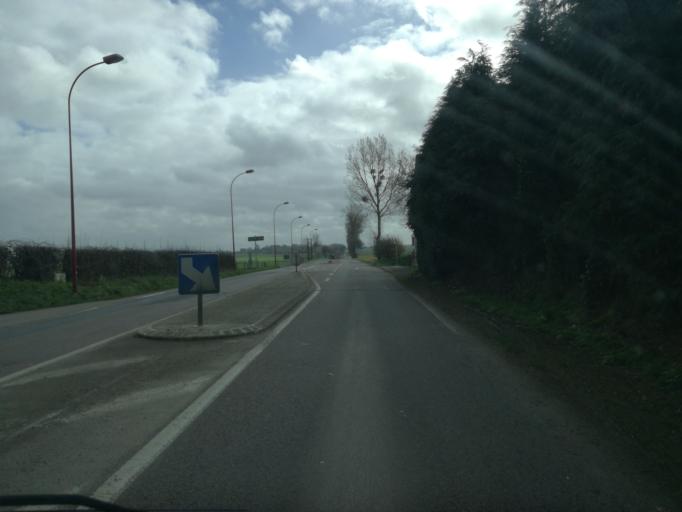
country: FR
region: Haute-Normandie
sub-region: Departement de la Seine-Maritime
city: Fauville-en-Caux
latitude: 49.6522
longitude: 0.6035
